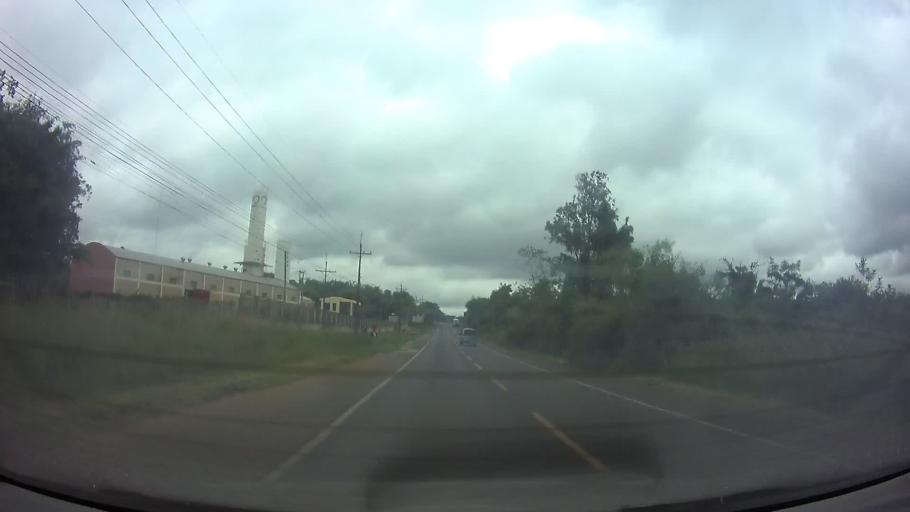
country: PY
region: Central
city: Guarambare
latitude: -25.4993
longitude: -57.4843
